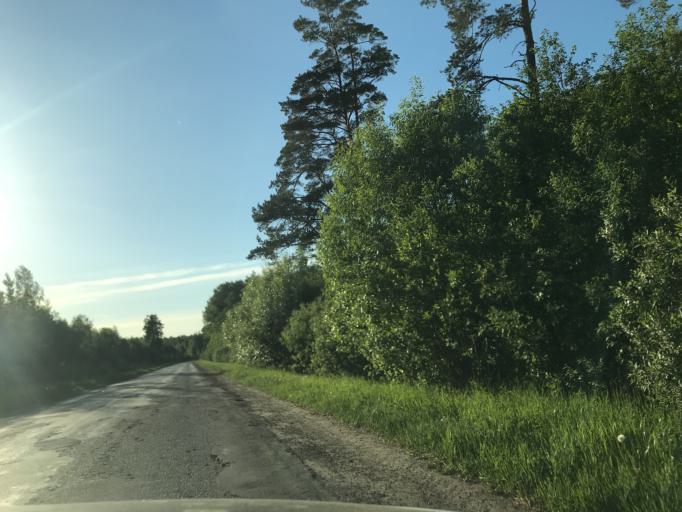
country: LV
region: Ozolnieku
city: Ozolnieki
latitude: 56.6022
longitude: 23.7972
